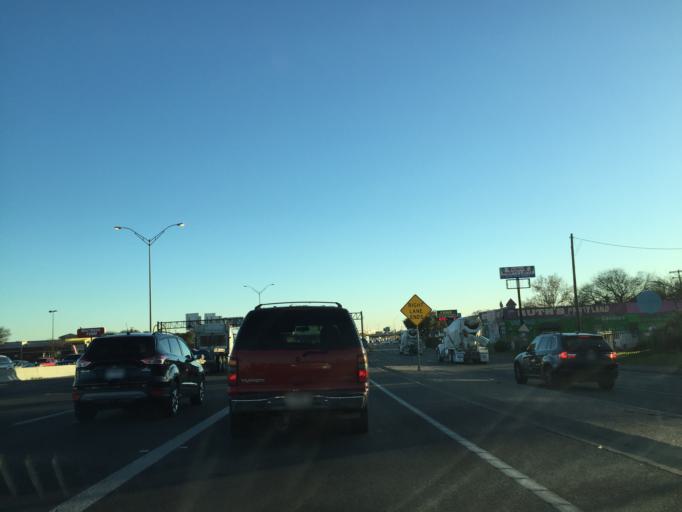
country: US
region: Texas
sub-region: Travis County
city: Austin
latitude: 30.3153
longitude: -97.7080
